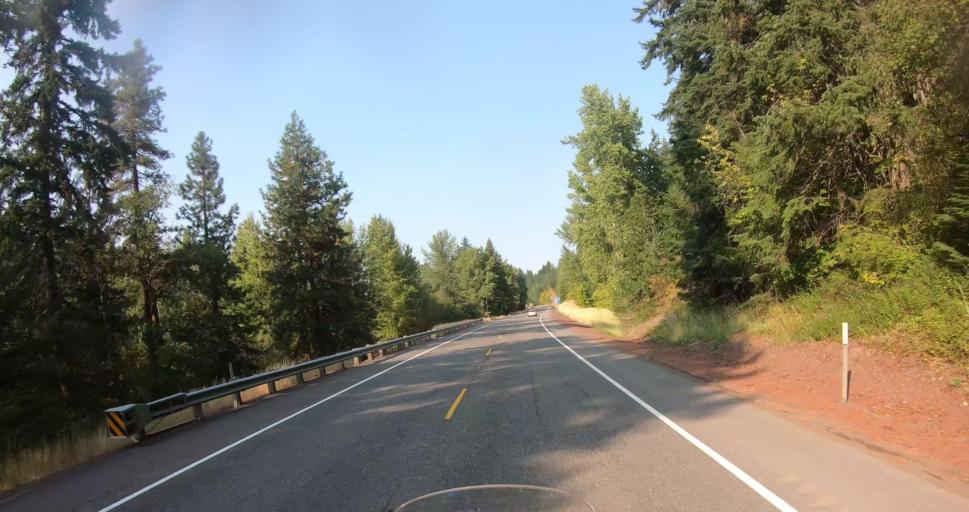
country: US
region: Oregon
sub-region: Hood River County
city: Odell
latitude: 45.4953
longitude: -121.5630
